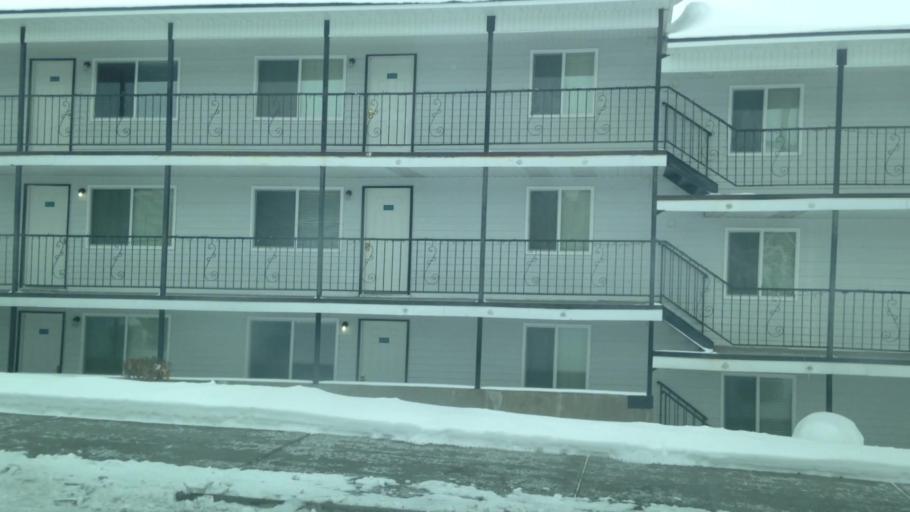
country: US
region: Idaho
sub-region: Madison County
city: Rexburg
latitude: 43.8168
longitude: -111.7874
